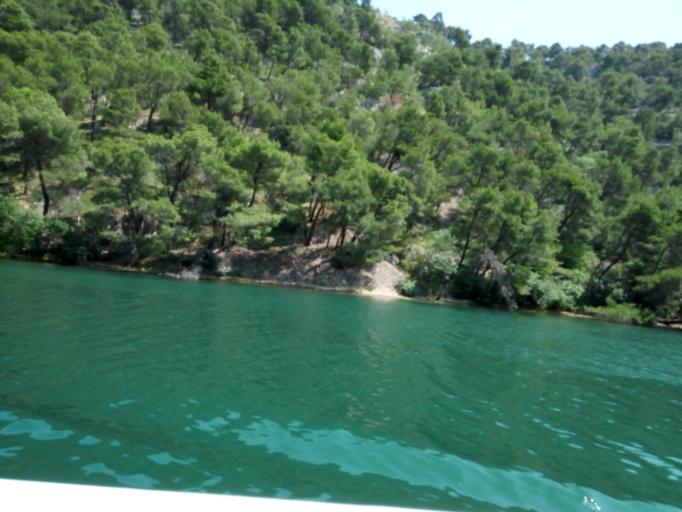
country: HR
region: Sibensko-Kniniska
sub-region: Grad Sibenik
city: Sibenik
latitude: 43.8193
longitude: 15.9360
